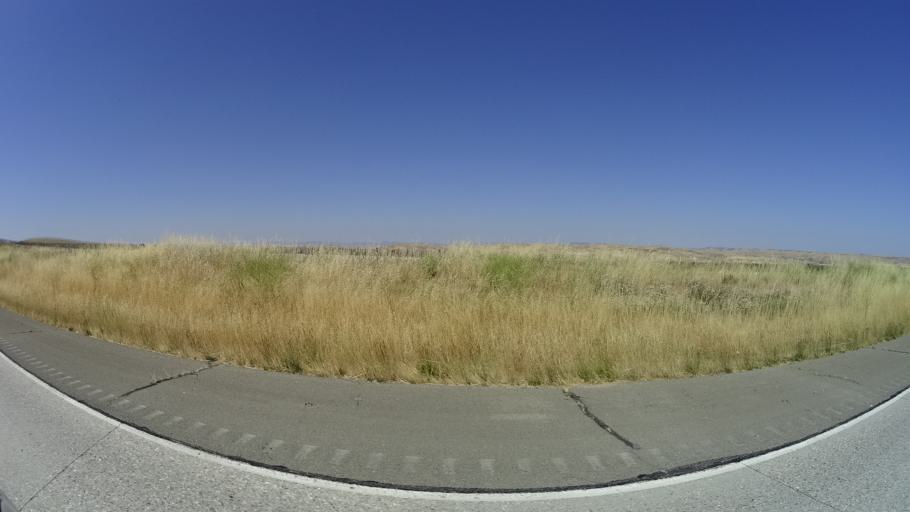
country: US
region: California
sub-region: Monterey County
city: King City
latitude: 36.0252
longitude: -120.9349
